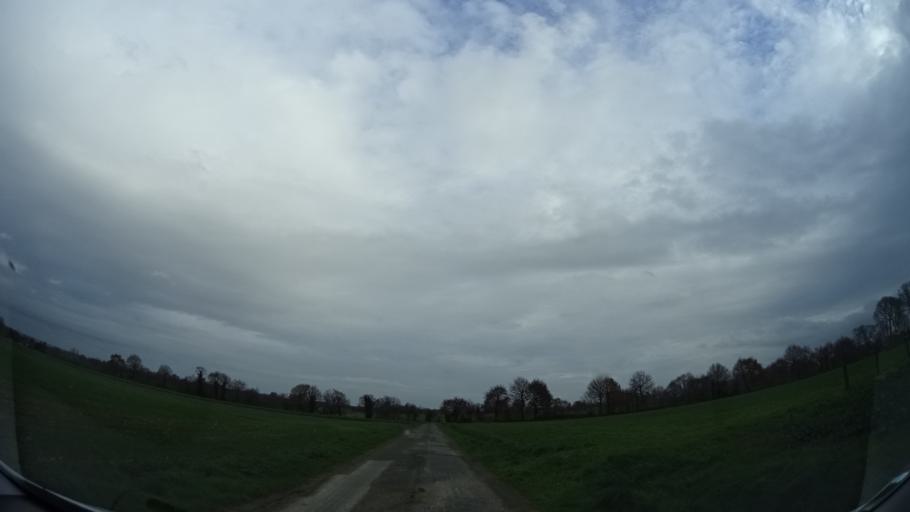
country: FR
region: Brittany
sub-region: Departement des Cotes-d'Armor
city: Evran
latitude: 48.3357
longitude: -1.9574
